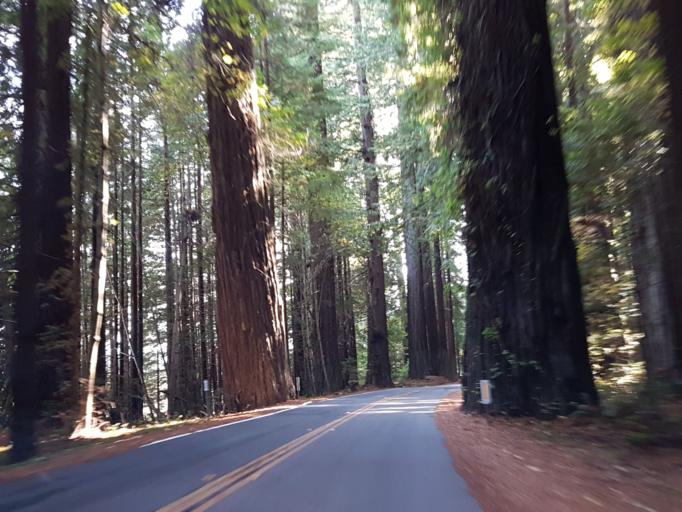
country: US
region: California
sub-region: Humboldt County
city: Rio Dell
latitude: 40.4415
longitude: -123.9855
